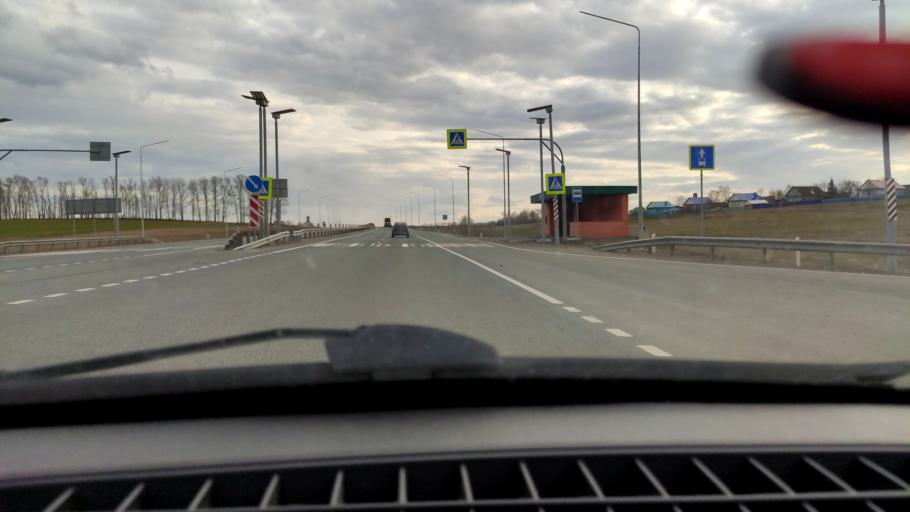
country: RU
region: Bashkortostan
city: Tolbazy
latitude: 54.0701
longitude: 55.8948
